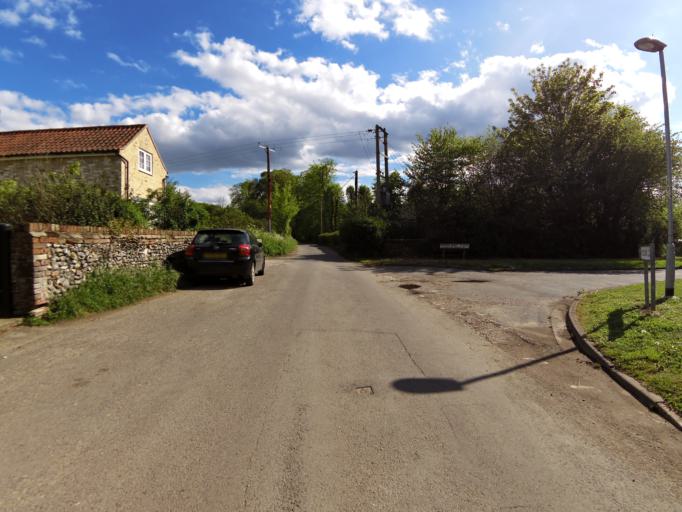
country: GB
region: England
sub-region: Suffolk
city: Thurston
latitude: 52.2487
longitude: 0.8239
